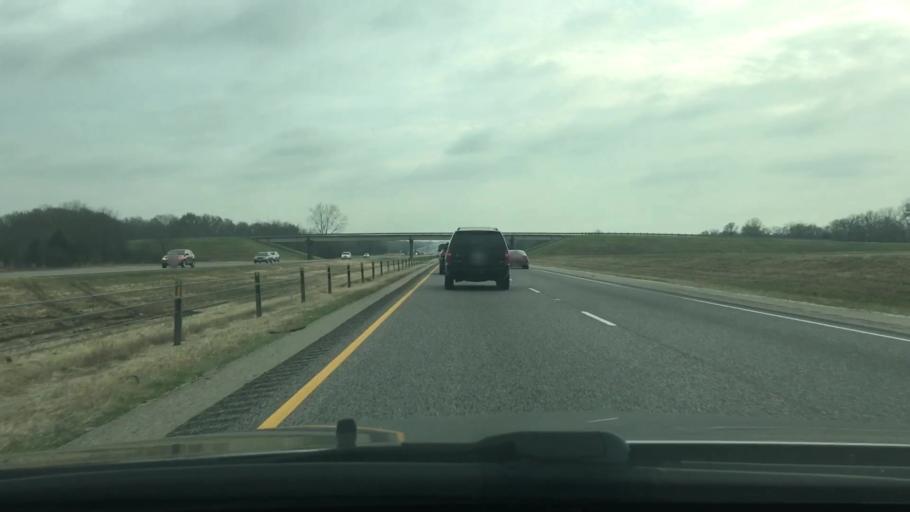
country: US
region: Texas
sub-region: Freestone County
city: Fairfield
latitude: 31.6378
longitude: -96.1585
